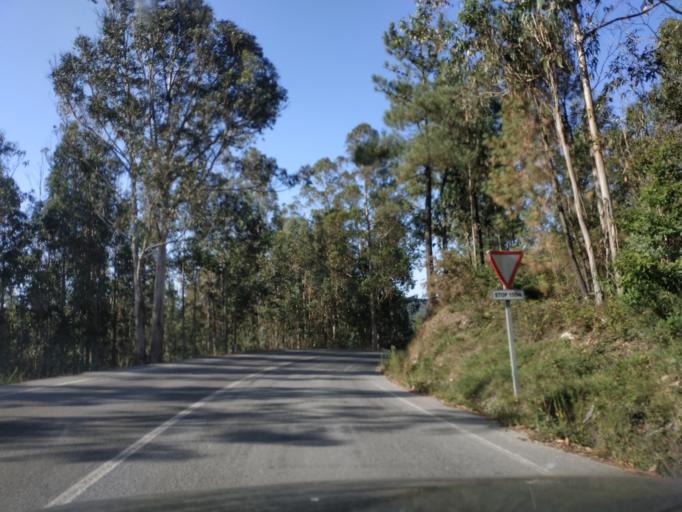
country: ES
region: Galicia
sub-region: Provincia da Coruna
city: Cerceda
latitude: 43.2331
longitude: -8.4645
